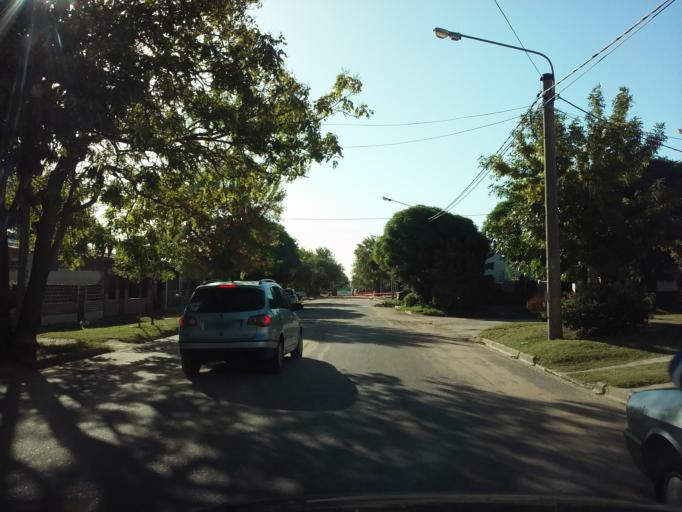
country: AR
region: La Pampa
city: Santa Rosa
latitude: -36.6401
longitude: -64.2996
